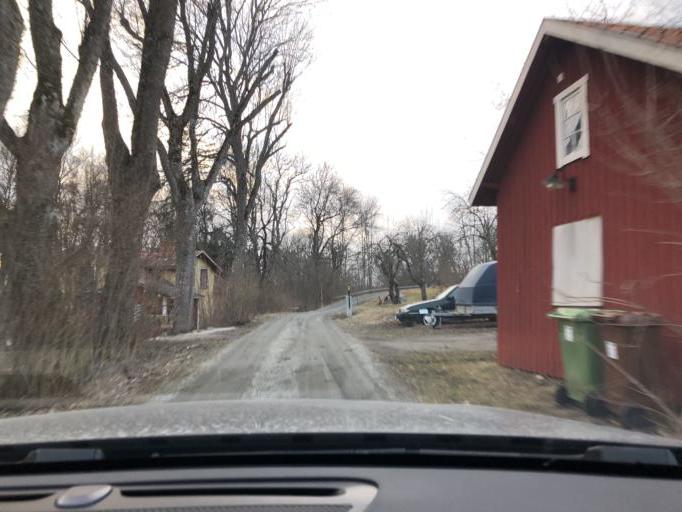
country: SE
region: Uppsala
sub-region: Uppsala Kommun
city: Gamla Uppsala
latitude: 59.9213
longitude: 17.6298
